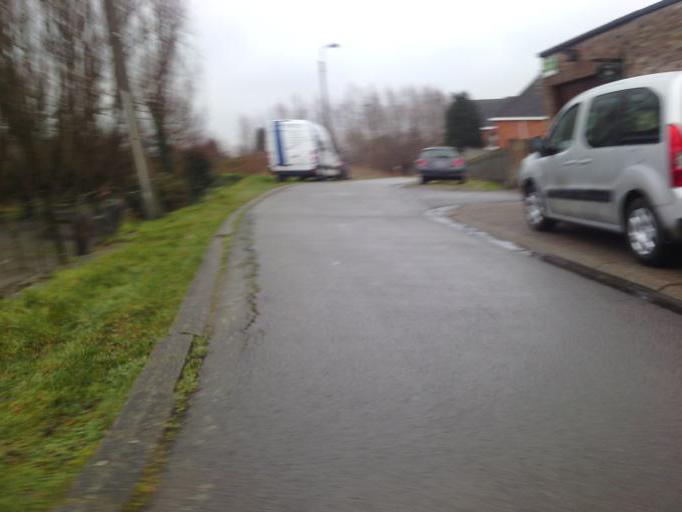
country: BE
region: Flanders
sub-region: Provincie Oost-Vlaanderen
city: Berlare
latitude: 51.0226
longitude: 4.0107
